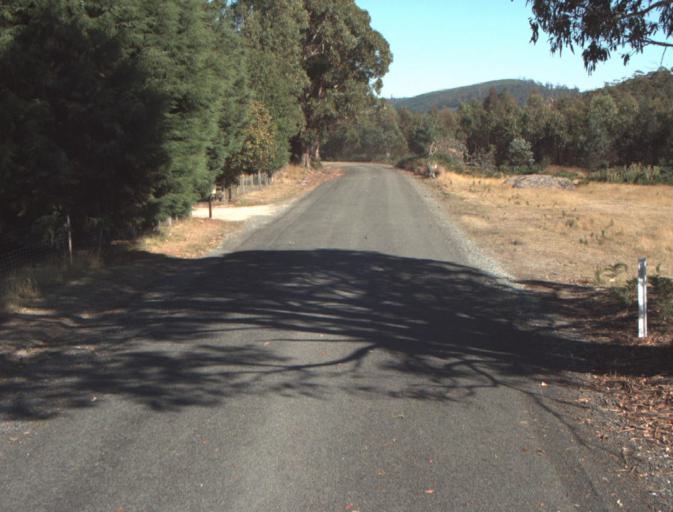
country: AU
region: Tasmania
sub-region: Dorset
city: Scottsdale
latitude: -41.2947
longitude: 147.3514
